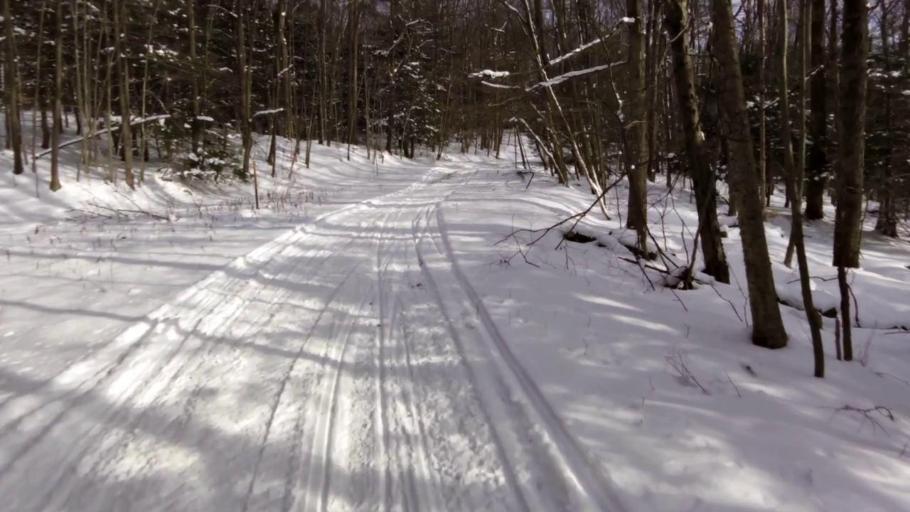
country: US
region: Pennsylvania
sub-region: McKean County
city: Foster Brook
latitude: 41.9996
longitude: -78.5337
